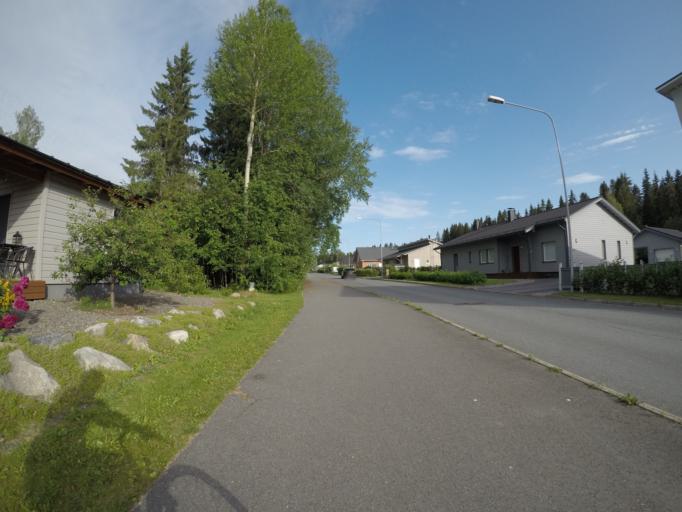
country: FI
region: Haeme
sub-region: Haemeenlinna
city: Parola
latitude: 60.9752
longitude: 24.3858
